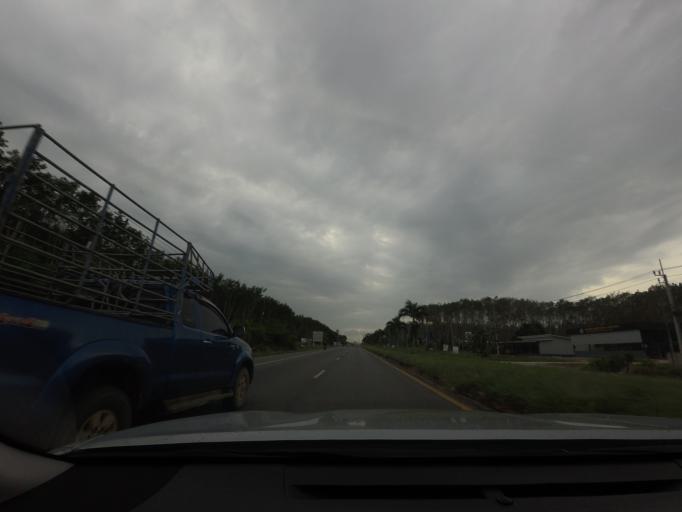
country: TH
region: Surat Thani
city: Phunphin
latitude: 9.0453
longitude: 99.1550
